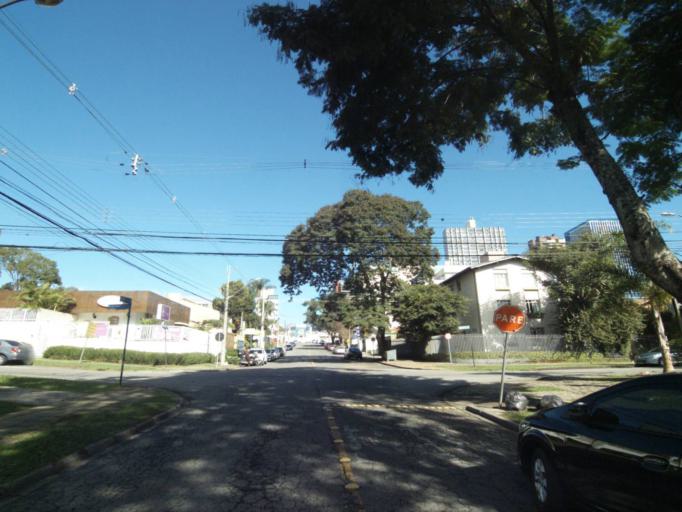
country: BR
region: Parana
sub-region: Curitiba
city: Curitiba
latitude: -25.4111
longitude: -49.2524
